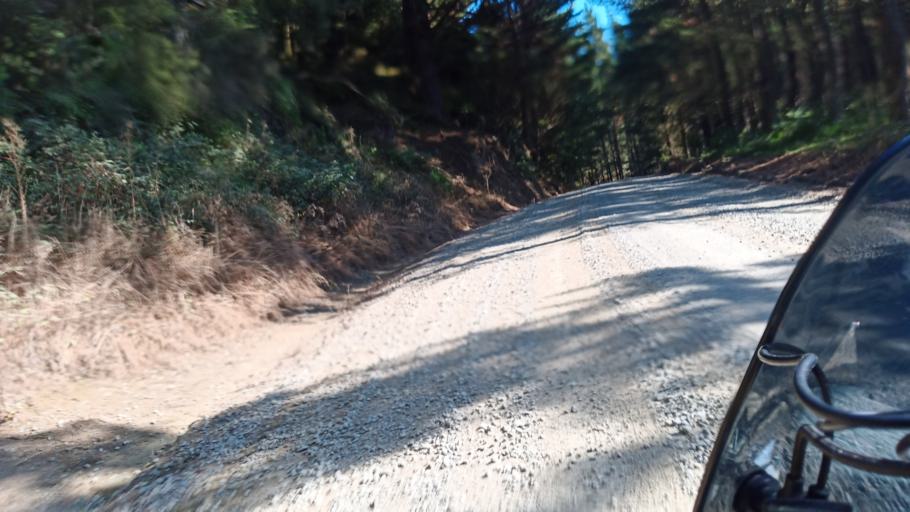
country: NZ
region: Hawke's Bay
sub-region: Wairoa District
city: Wairoa
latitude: -38.9312
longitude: 177.2270
